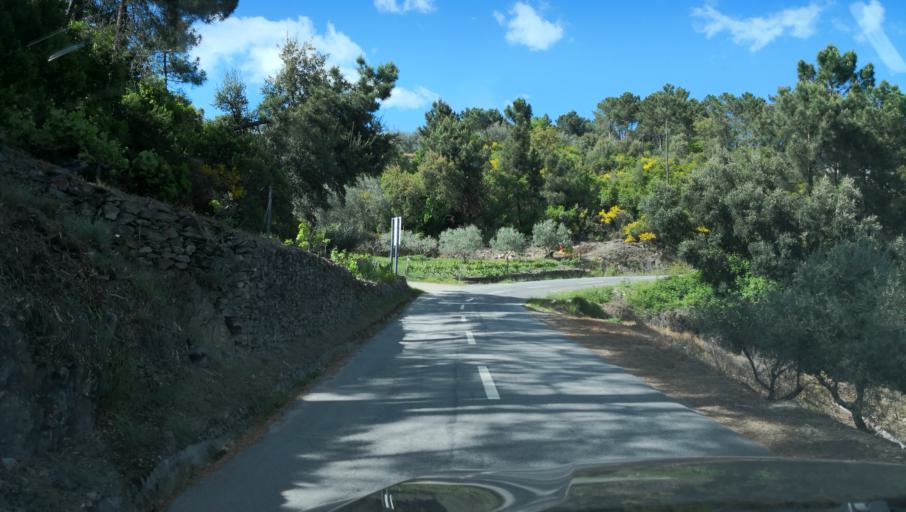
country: PT
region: Vila Real
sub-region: Vila Real
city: Vila Real
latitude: 41.2507
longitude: -7.7364
